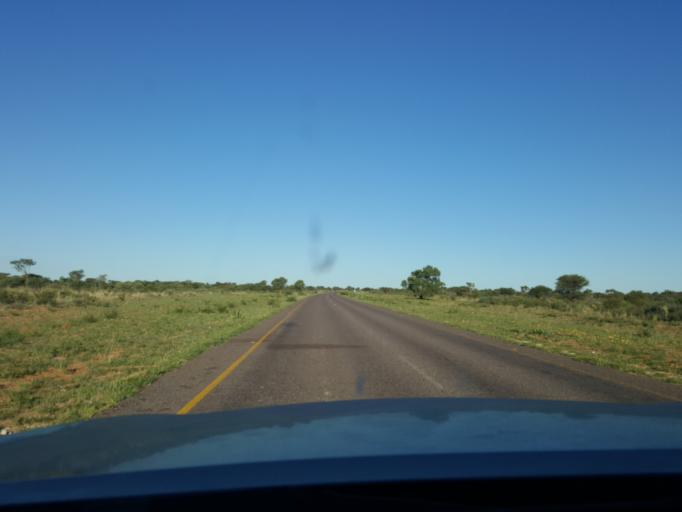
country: BW
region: Southern
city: Khakhea
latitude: -24.3022
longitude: 23.3942
